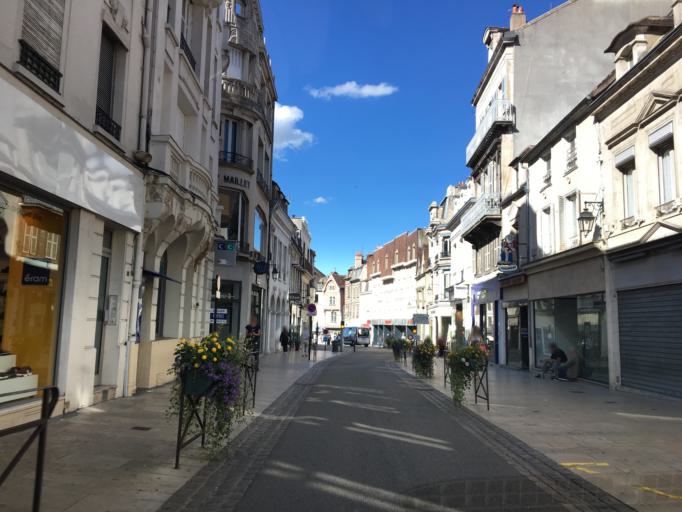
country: FR
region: Bourgogne
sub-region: Departement de l'Yonne
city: Auxerre
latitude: 47.7940
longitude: 3.5691
